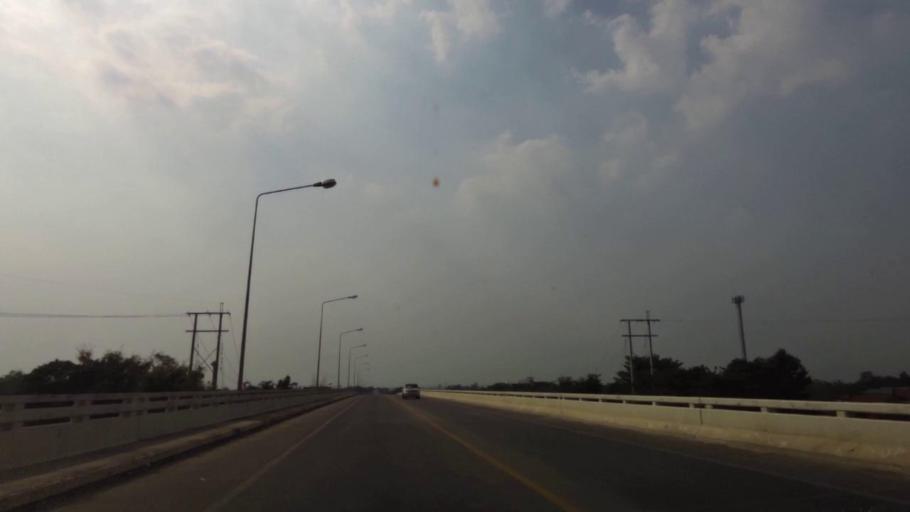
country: TH
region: Phra Nakhon Si Ayutthaya
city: Phra Nakhon Si Ayutthaya
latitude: 14.3040
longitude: 100.5658
